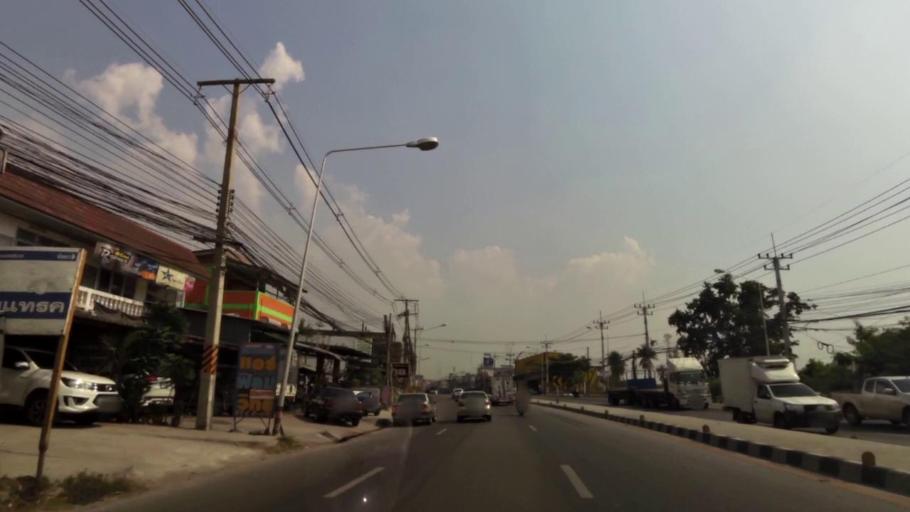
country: TH
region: Chon Buri
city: Chon Buri
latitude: 13.3499
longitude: 101.0119
